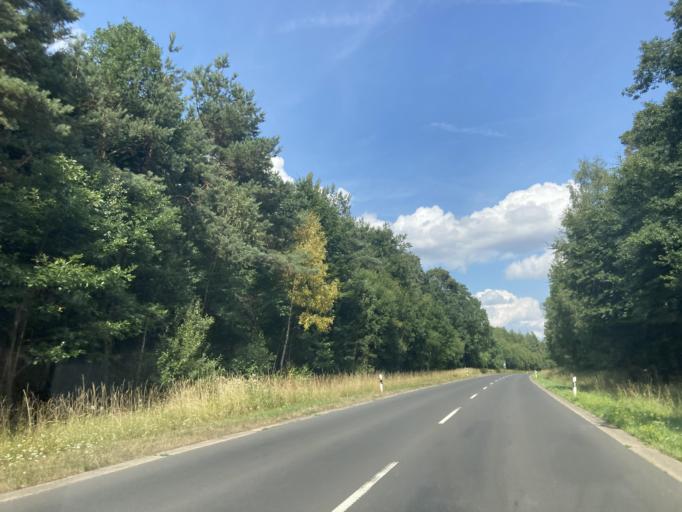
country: DE
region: Hesse
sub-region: Regierungsbezirk Kassel
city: Grossenluder
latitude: 50.5425
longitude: 9.5537
